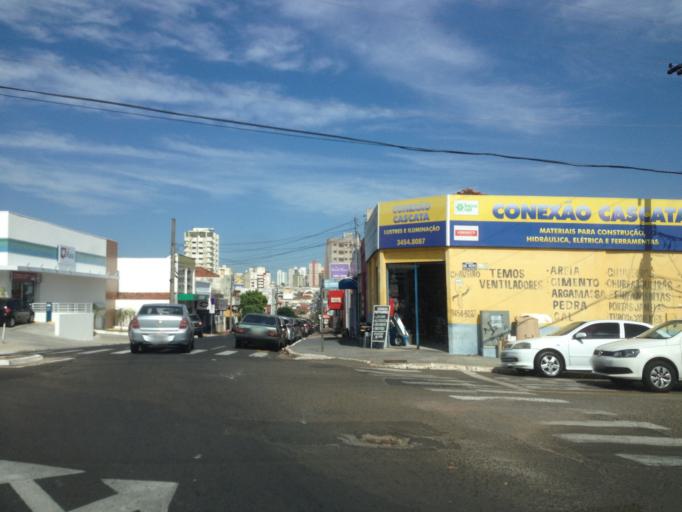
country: BR
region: Sao Paulo
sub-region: Marilia
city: Marilia
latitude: -22.2116
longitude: -49.9391
